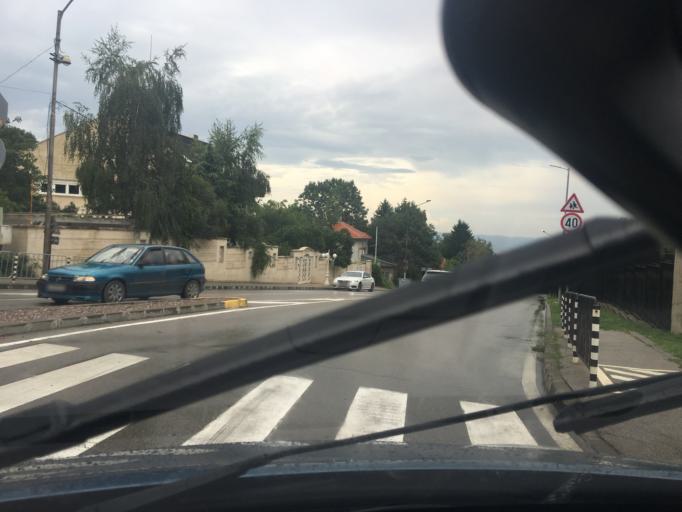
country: BG
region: Sofia-Capital
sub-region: Stolichna Obshtina
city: Sofia
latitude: 42.6496
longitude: 23.2658
